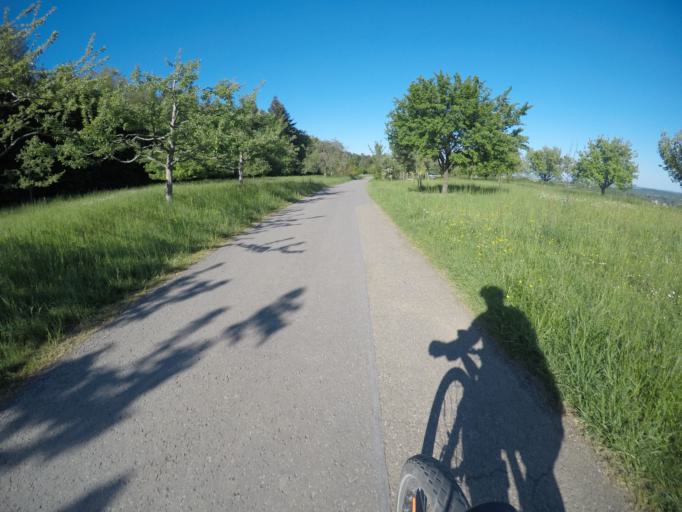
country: DE
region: Baden-Wuerttemberg
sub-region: Regierungsbezirk Stuttgart
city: Weissach
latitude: 48.8567
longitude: 8.9030
